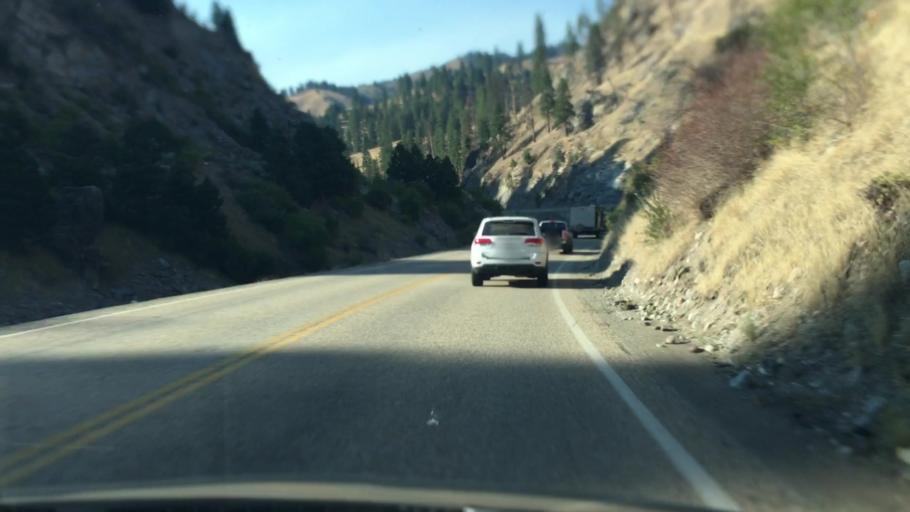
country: US
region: Idaho
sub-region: Boise County
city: Idaho City
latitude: 44.1014
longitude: -116.0952
